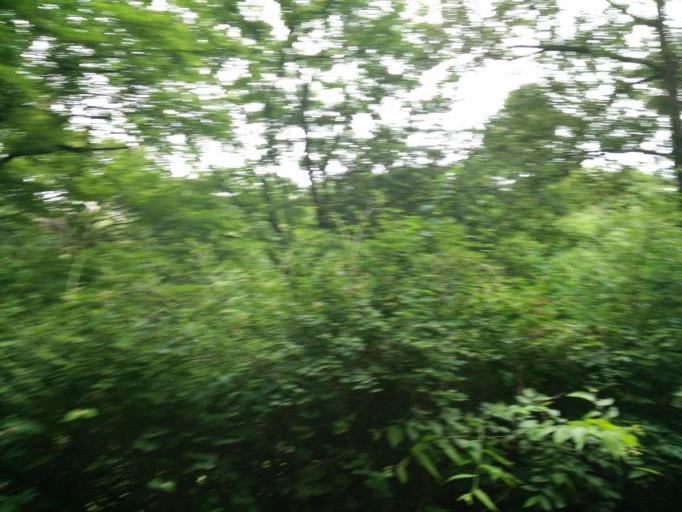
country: BE
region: Flanders
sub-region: Provincie Antwerpen
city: Antwerpen
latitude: 51.2115
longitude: 4.4157
